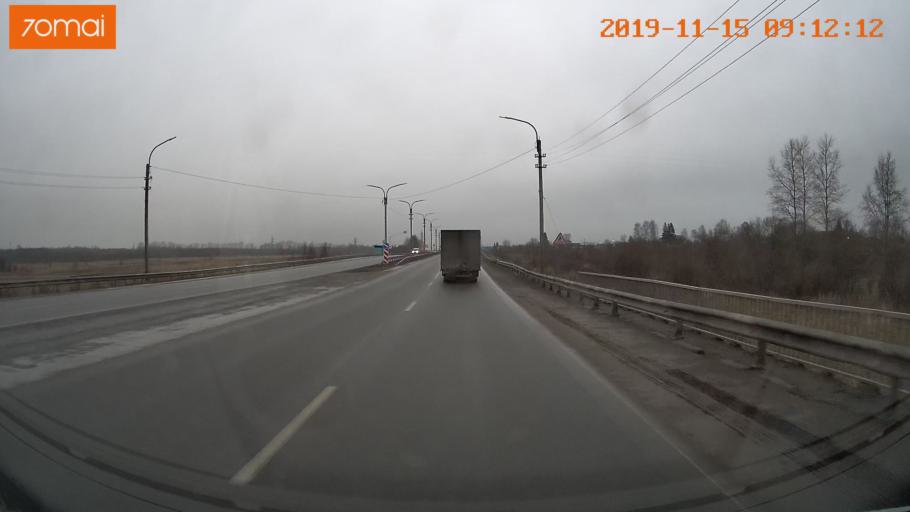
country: RU
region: Vologda
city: Tonshalovo
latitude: 59.2055
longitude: 37.9395
